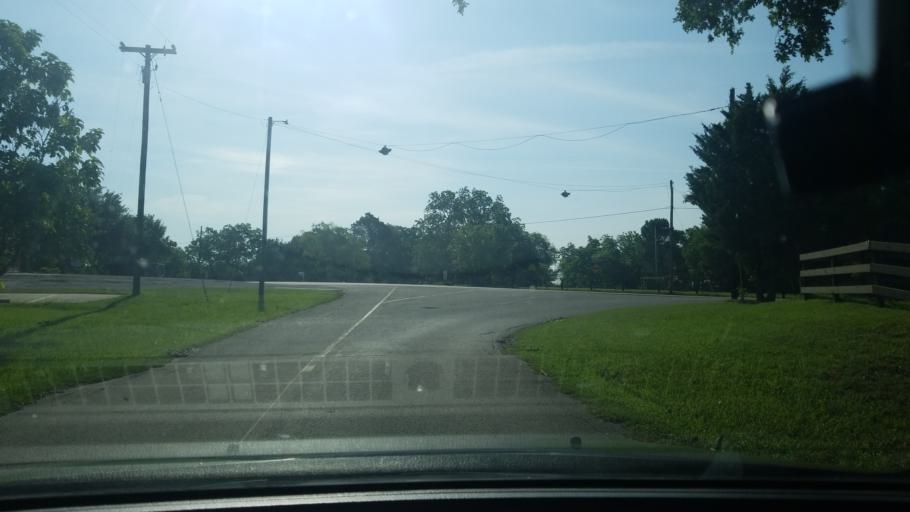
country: US
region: Texas
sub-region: Dallas County
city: Sunnyvale
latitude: 32.7804
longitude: -96.5533
